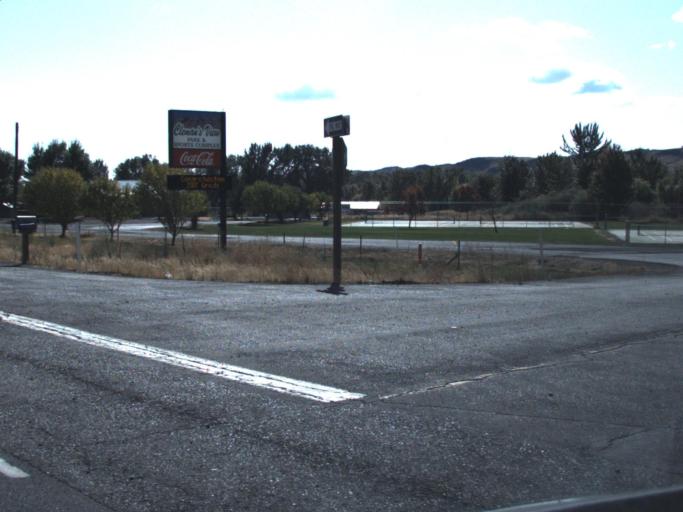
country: US
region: Washington
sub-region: Yakima County
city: Tieton
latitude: 46.7179
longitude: -120.6789
